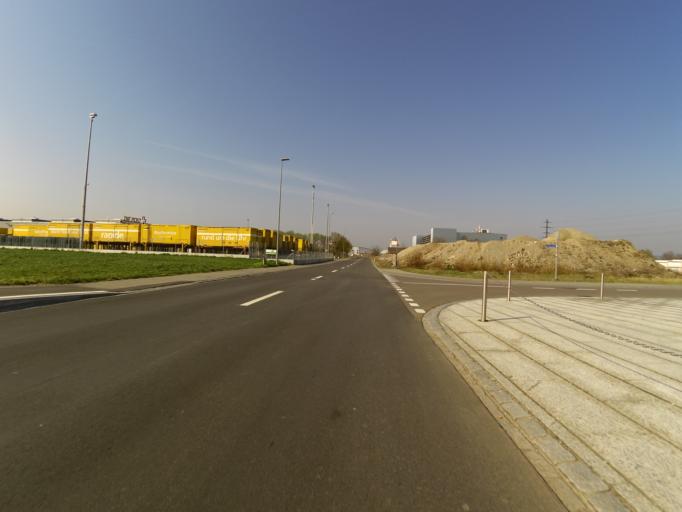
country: CH
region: Thurgau
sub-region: Frauenfeld District
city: Frauenfeld
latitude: 47.5736
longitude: 8.9193
